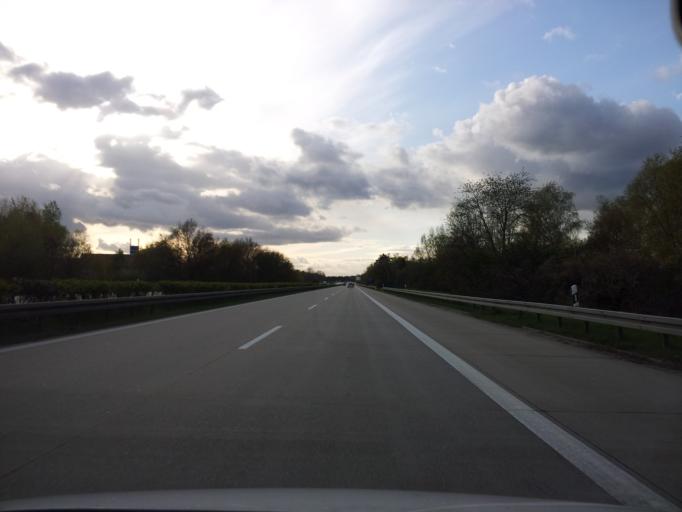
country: DE
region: Brandenburg
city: Cottbus
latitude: 51.7203
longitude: 14.3163
